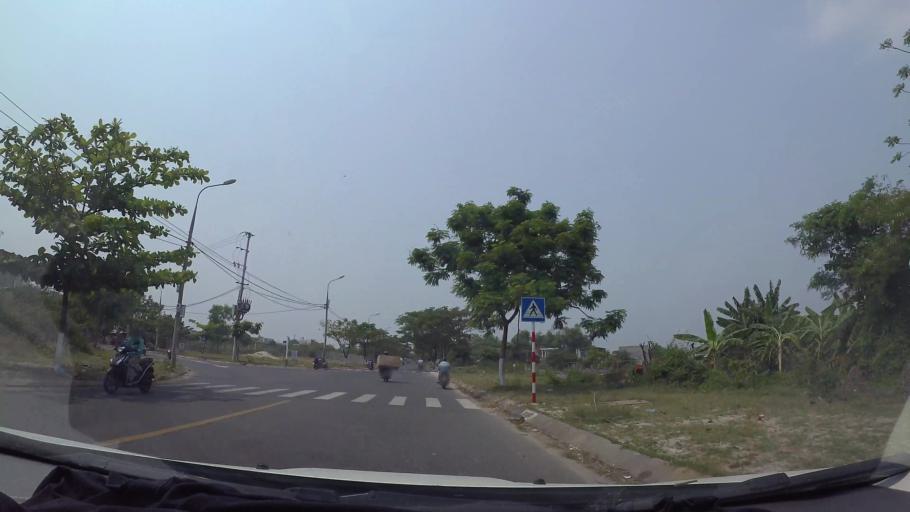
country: VN
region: Da Nang
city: Cam Le
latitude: 16.0079
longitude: 108.2128
